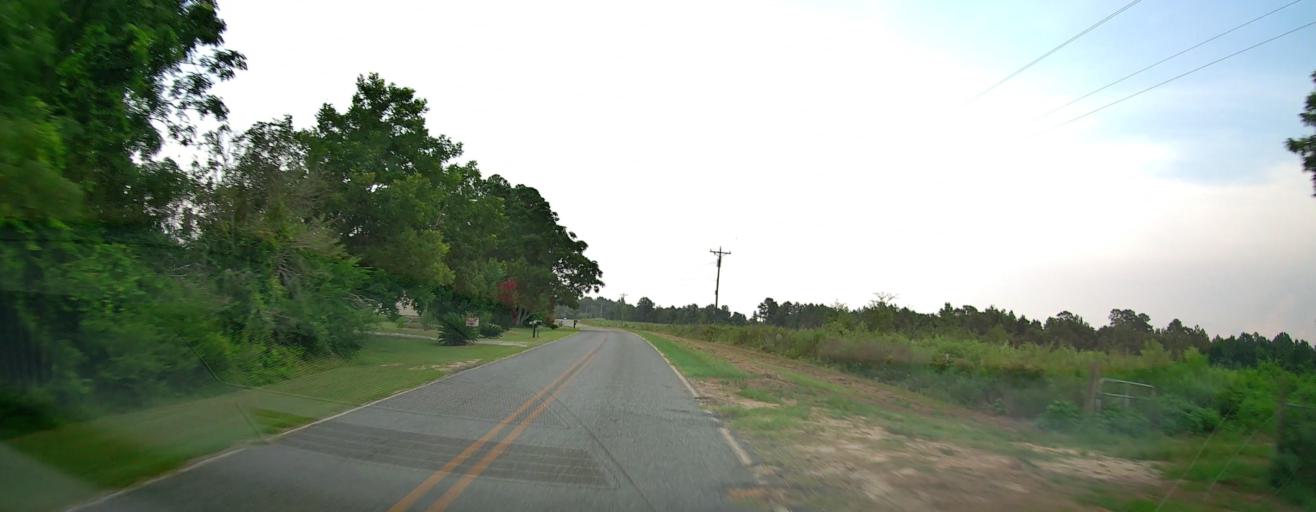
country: US
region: Georgia
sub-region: Laurens County
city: East Dublin
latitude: 32.6414
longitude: -82.8300
